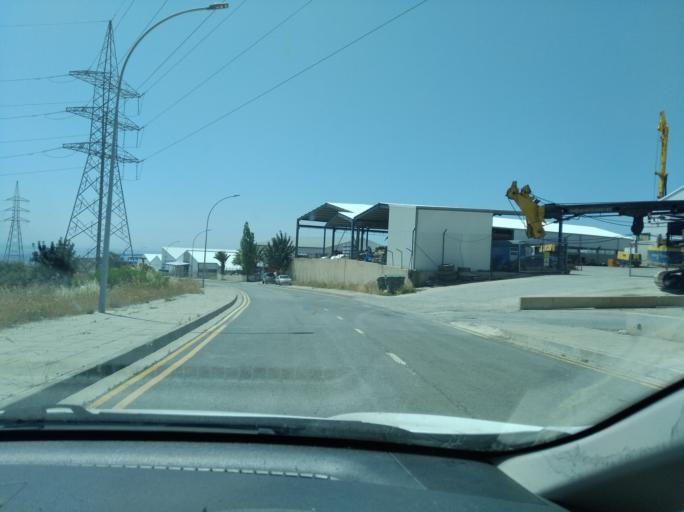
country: CY
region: Limassol
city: Ypsonas
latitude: 34.7337
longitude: 32.9443
